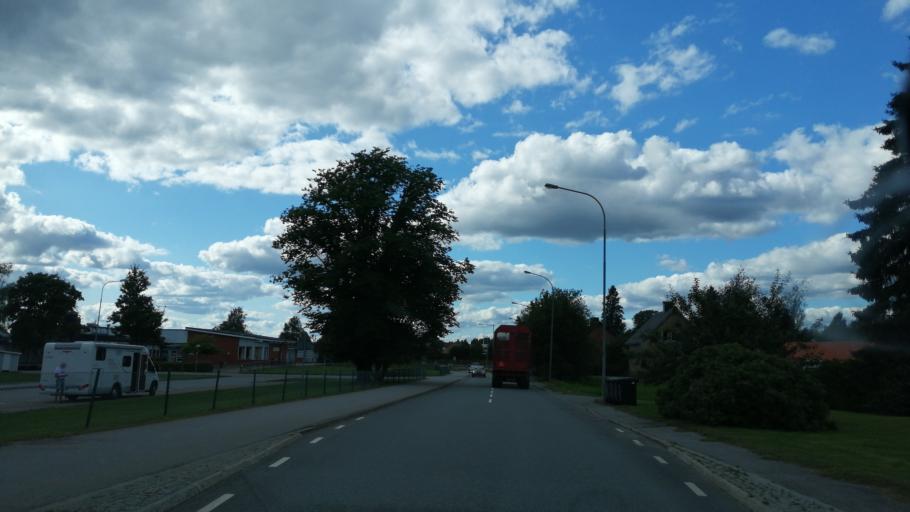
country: SE
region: Joenkoeping
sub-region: Gislaveds Kommun
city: Reftele
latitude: 57.1717
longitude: 13.6012
